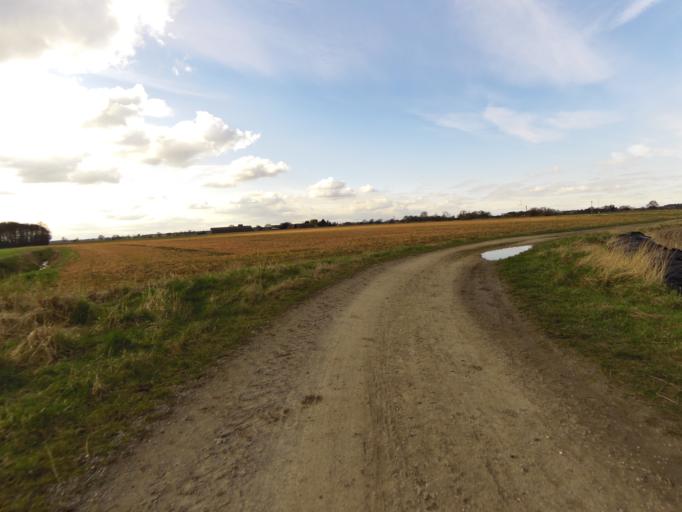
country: GB
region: England
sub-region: East Riding of Yorkshire
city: Pollington
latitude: 53.6556
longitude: -1.0664
